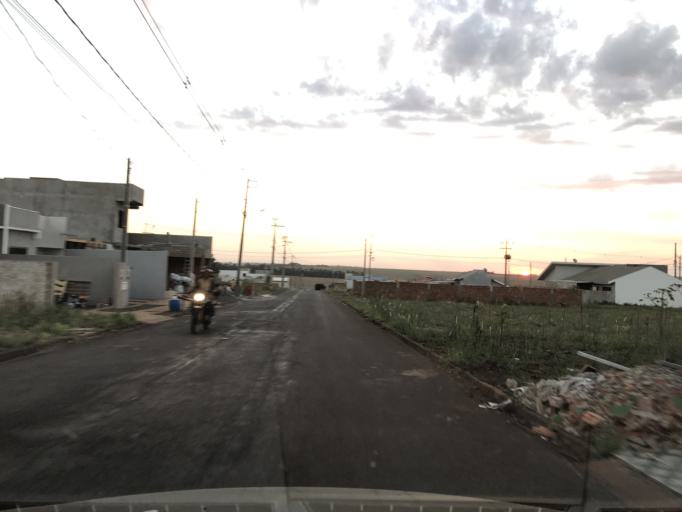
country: BR
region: Parana
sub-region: Palotina
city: Palotina
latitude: -24.3083
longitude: -53.8371
